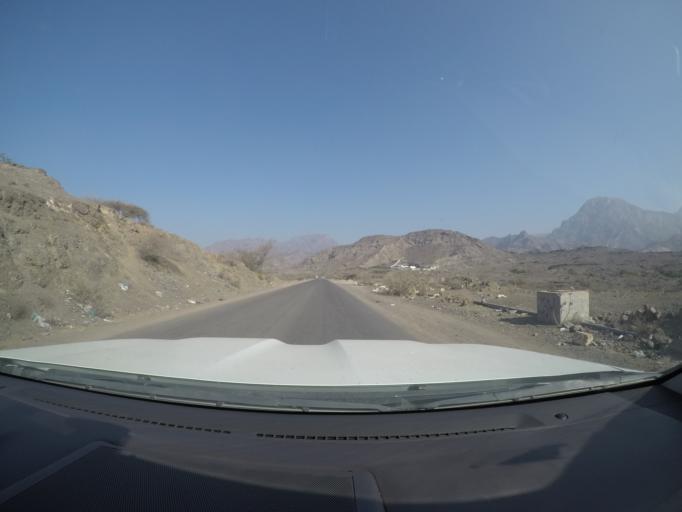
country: YE
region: Lahij
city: Habil ar Raydah
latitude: 13.6537
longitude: 44.8454
